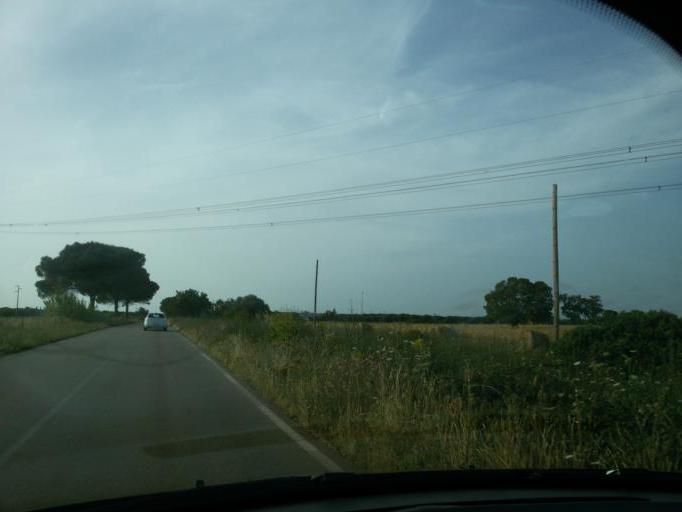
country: IT
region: Apulia
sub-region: Provincia di Brindisi
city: San Pancrazio Salentino
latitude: 40.3419
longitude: 17.8484
